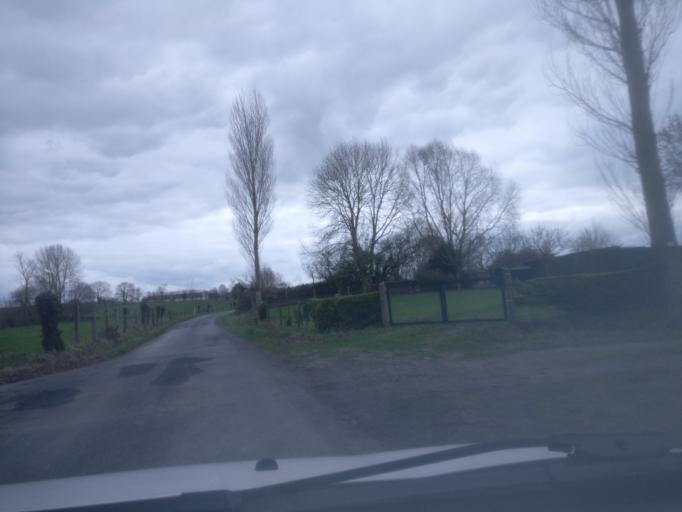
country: FR
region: Lower Normandy
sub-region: Departement de la Manche
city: Marcey-les-Greves
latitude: 48.6704
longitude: -1.4198
